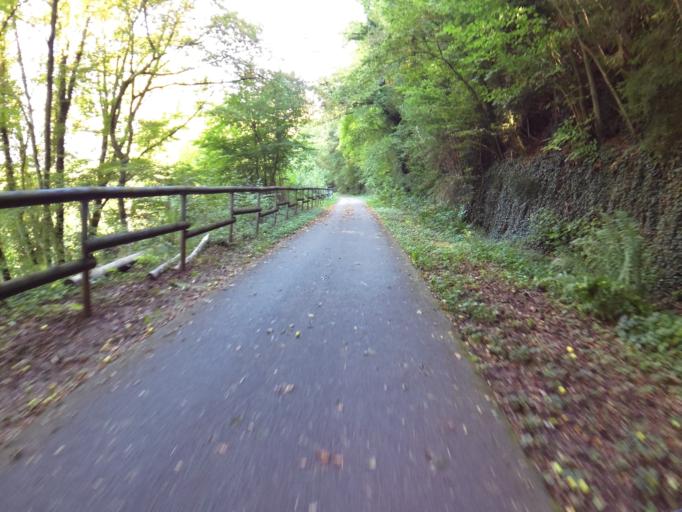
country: LU
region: Grevenmacher
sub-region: Canton d'Echternach
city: Rosport
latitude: 49.7609
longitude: 6.5185
